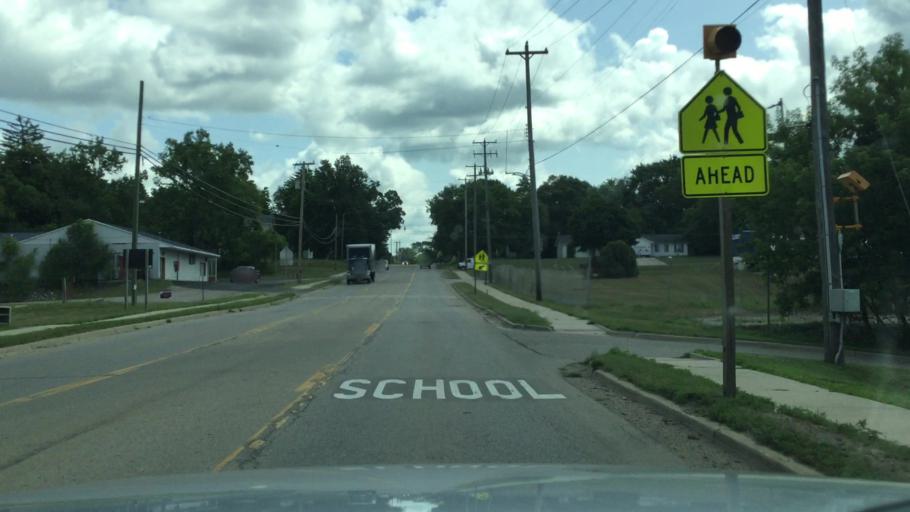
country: US
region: Michigan
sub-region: Montcalm County
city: Greenville
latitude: 43.1775
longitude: -85.2471
